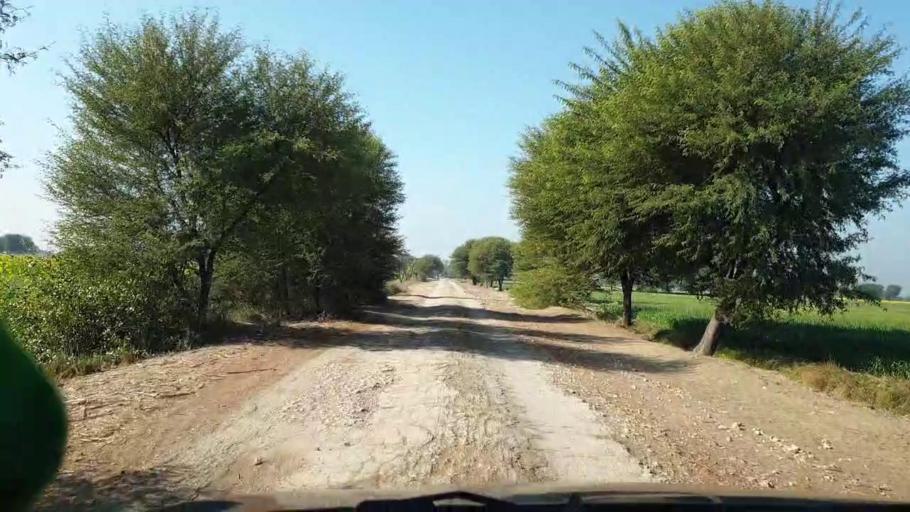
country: PK
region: Sindh
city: Sinjhoro
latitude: 25.9988
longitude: 68.7628
